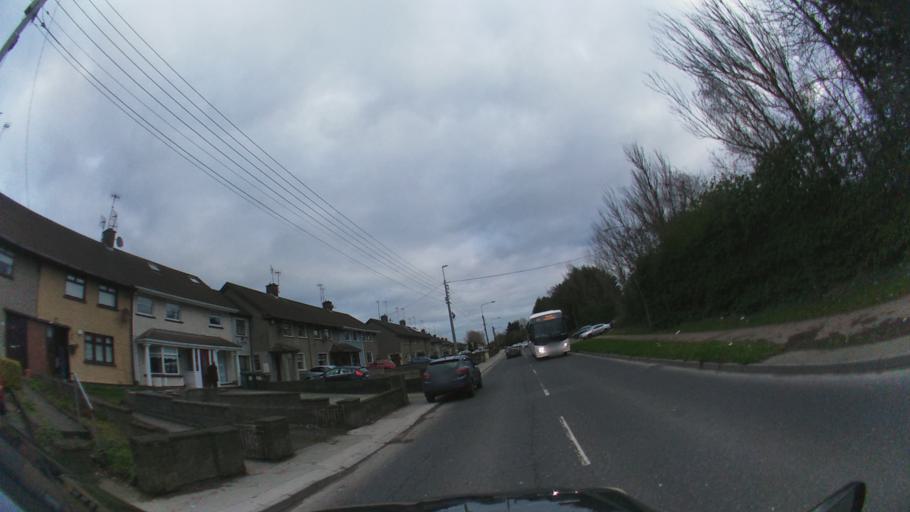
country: IE
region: Leinster
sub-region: Lu
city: Drogheda
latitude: 53.7087
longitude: -6.3653
